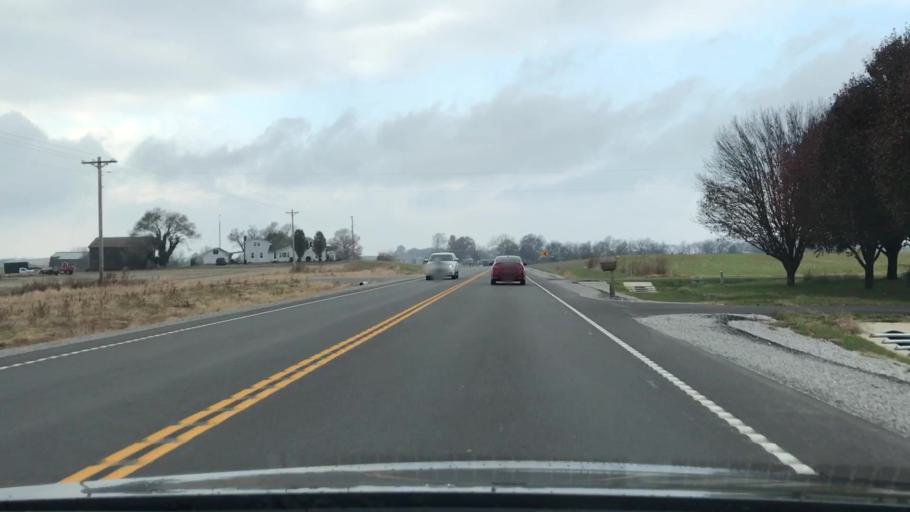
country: US
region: Kentucky
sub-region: Simpson County
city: Franklin
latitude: 36.7112
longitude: -86.5019
